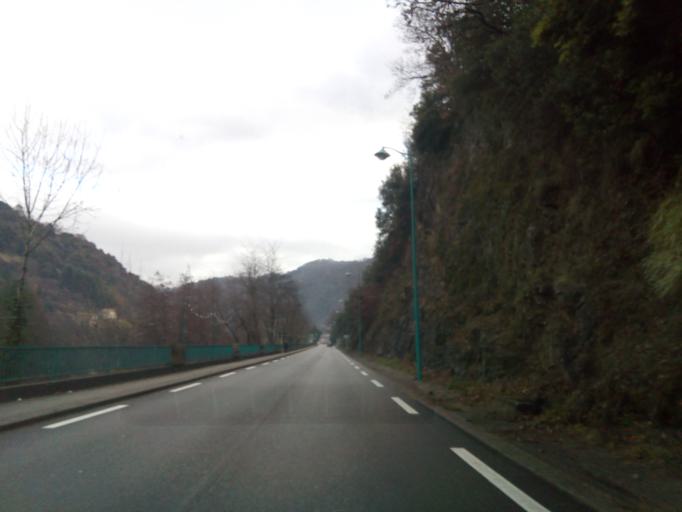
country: FR
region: Rhone-Alpes
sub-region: Departement de l'Ardeche
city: Saint-Sauveur-de-Montagut
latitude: 44.8198
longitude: 4.5892
